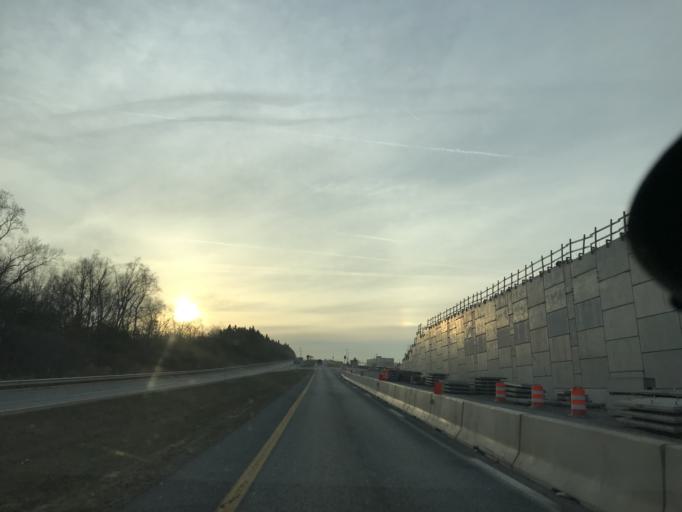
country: US
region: Maryland
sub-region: Prince George's County
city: Woodlawn
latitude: 38.9563
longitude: -76.8903
